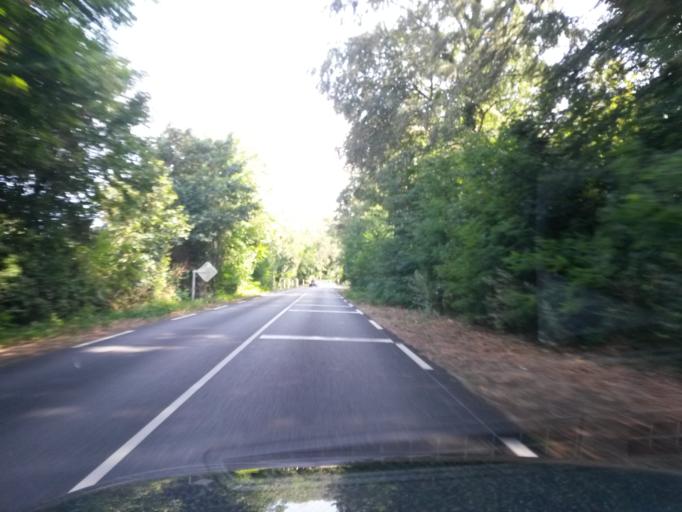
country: FR
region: Pays de la Loire
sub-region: Departement de la Vendee
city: Olonne-sur-Mer
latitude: 46.5598
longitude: -1.8110
